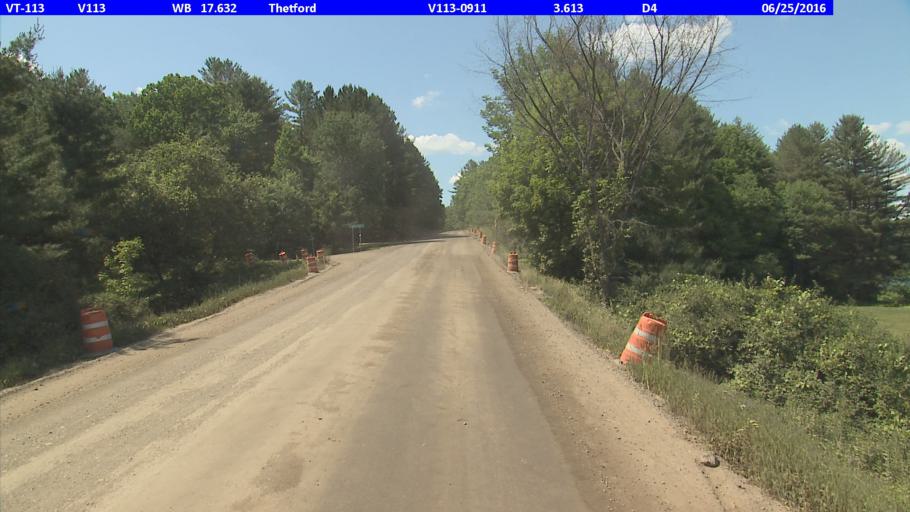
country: US
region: New Hampshire
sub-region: Grafton County
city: Lyme
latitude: 43.8480
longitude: -72.2539
